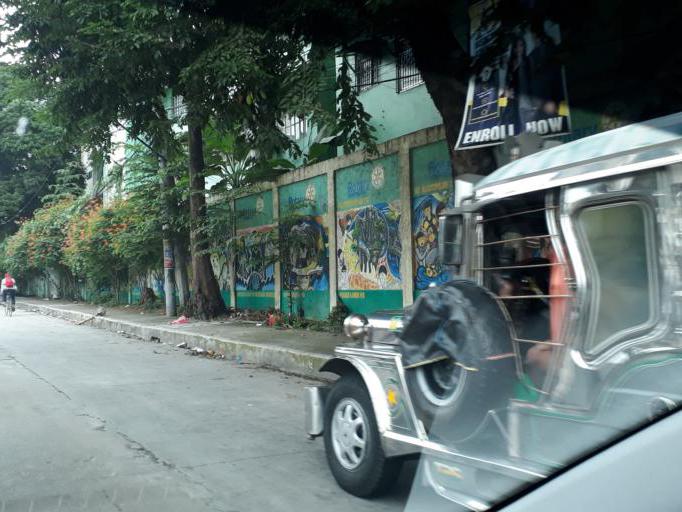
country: PH
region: Calabarzon
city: Del Monte
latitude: 14.6334
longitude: 120.9949
